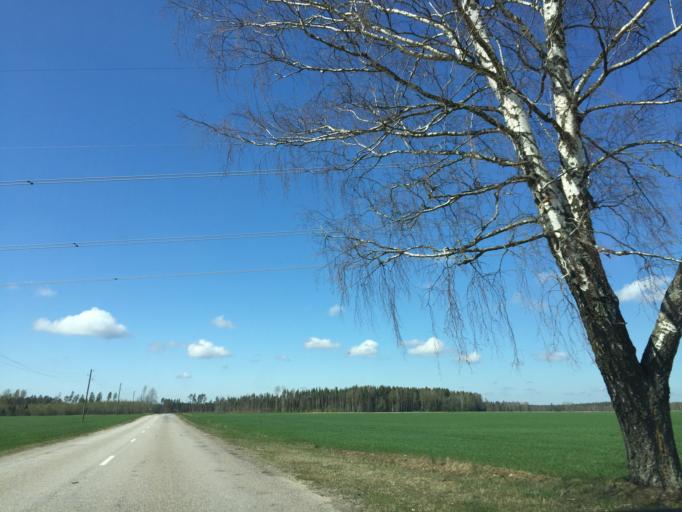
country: LV
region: Strenci
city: Seda
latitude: 57.5789
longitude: 25.7607
